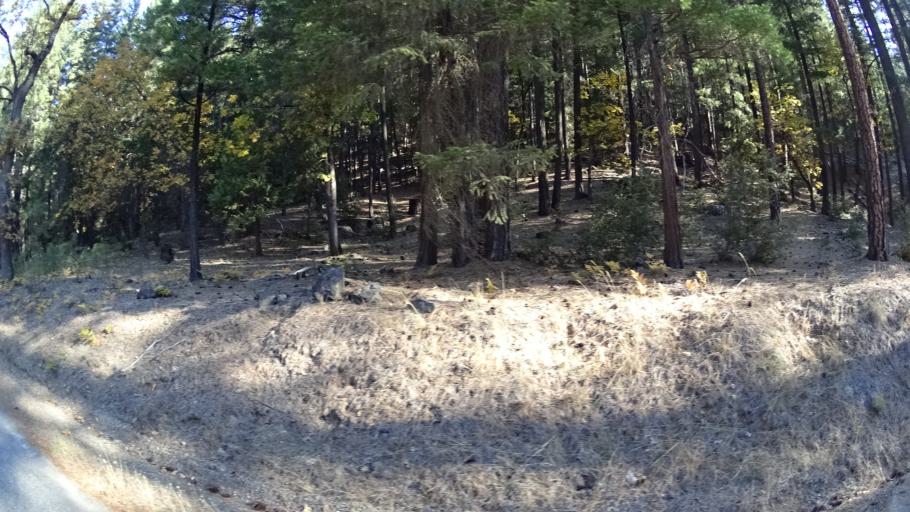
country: US
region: California
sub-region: Siskiyou County
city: Happy Camp
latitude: 41.6349
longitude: -123.1042
